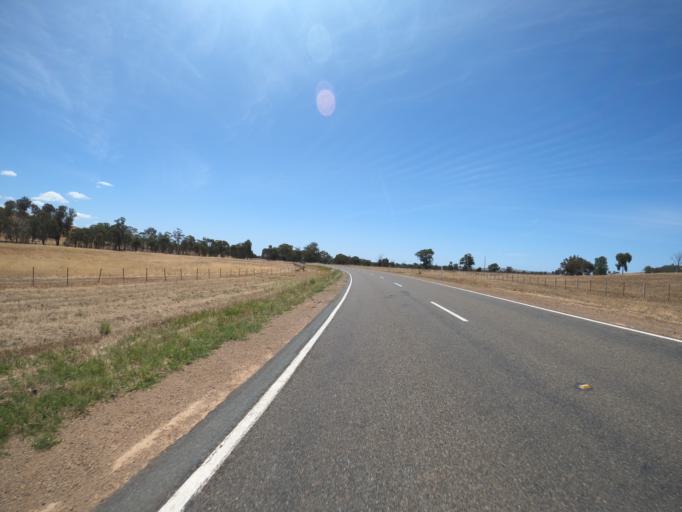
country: AU
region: Victoria
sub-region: Benalla
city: Benalla
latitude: -36.3308
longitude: 145.9613
